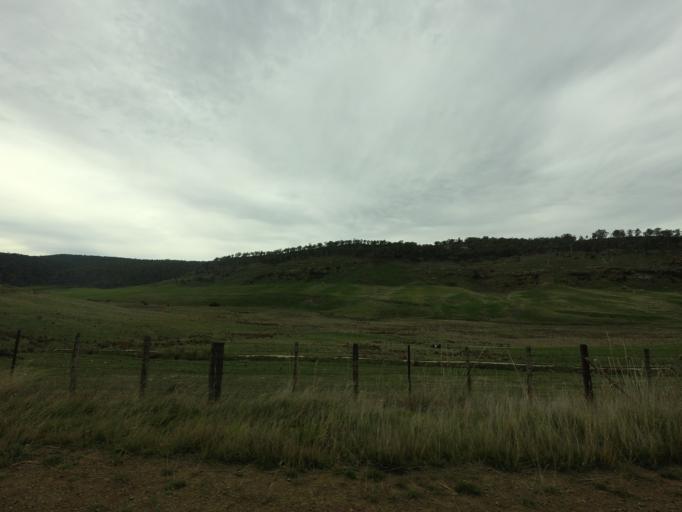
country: AU
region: Tasmania
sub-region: Derwent Valley
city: New Norfolk
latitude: -42.4010
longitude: 146.9192
